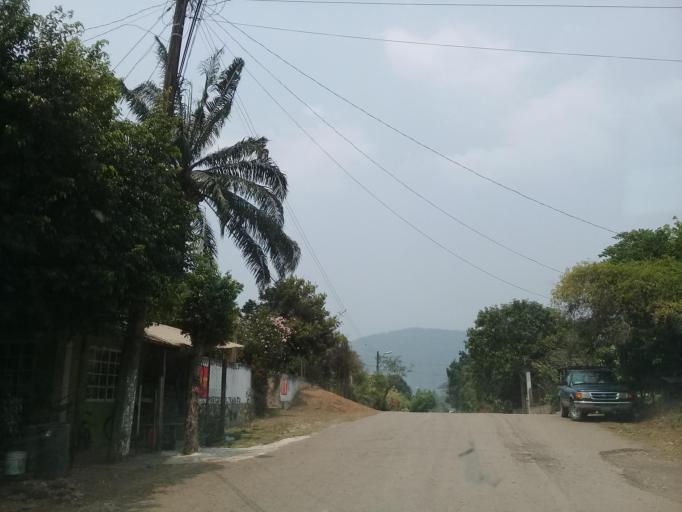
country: MX
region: Veracruz
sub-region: Tezonapa
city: Laguna Chica (Pueblo Nuevo)
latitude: 18.5457
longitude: -96.7342
